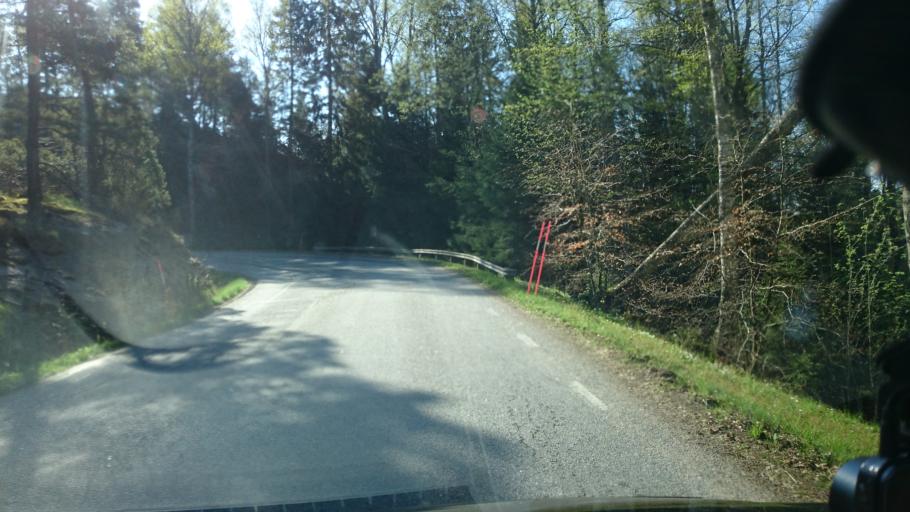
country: SE
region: Vaestra Goetaland
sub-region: Orust
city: Henan
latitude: 58.3505
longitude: 11.6914
